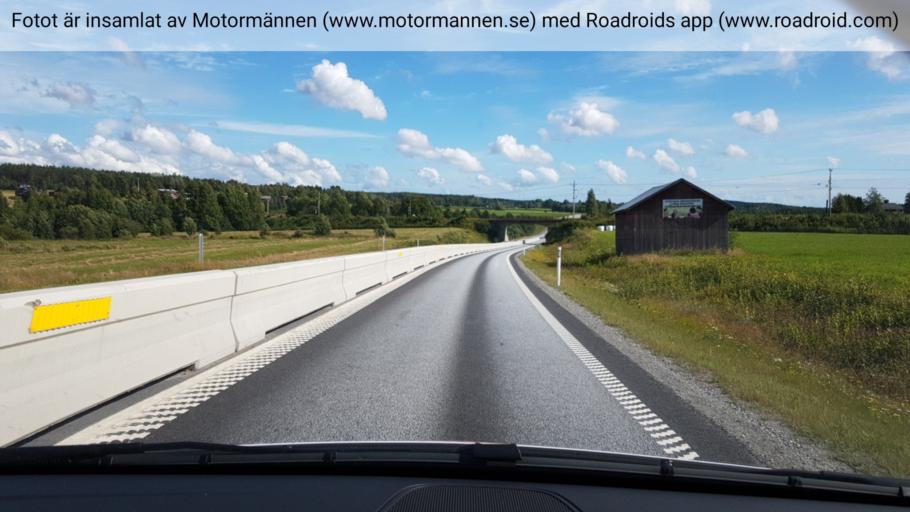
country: SE
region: Vaesterbotten
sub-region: Umea Kommun
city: Roback
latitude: 63.8866
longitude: 20.0226
